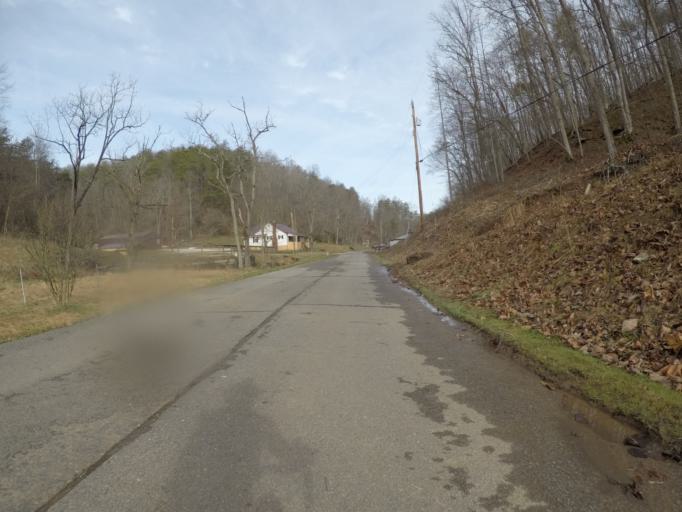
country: US
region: West Virginia
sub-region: Wayne County
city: Lavalette
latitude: 38.3319
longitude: -82.3779
